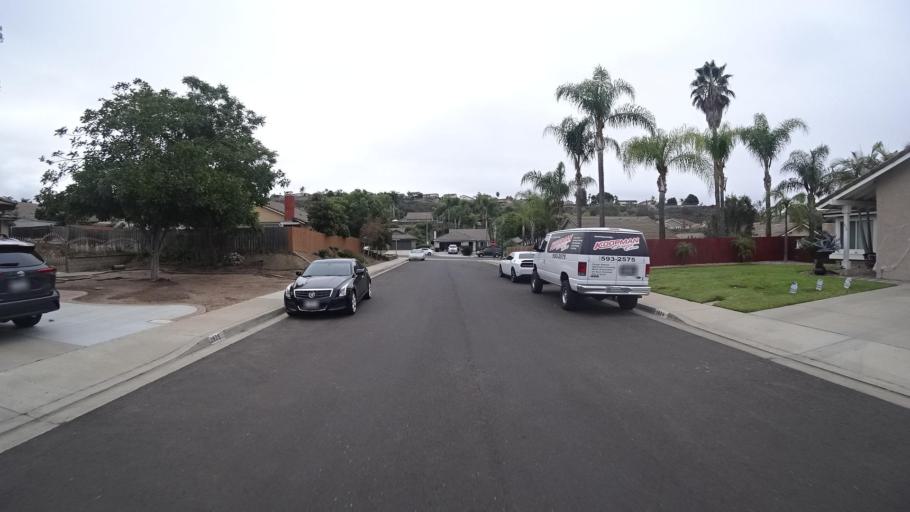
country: US
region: California
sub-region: San Diego County
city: Rancho San Diego
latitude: 32.7568
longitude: -116.9153
